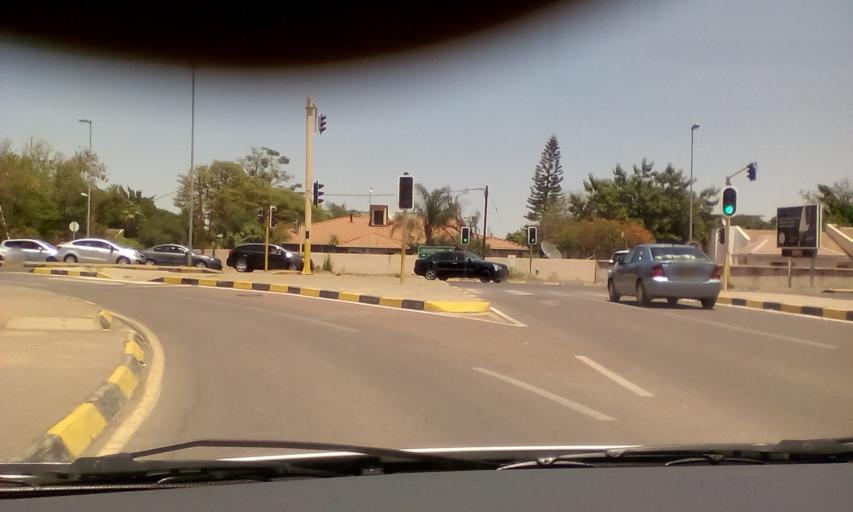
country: BW
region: South East
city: Gaborone
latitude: -24.6515
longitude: 25.9028
